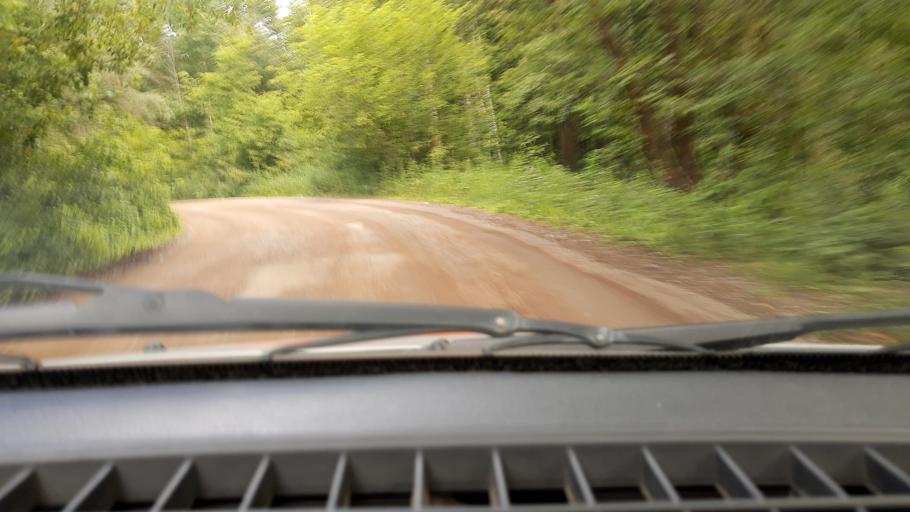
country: RU
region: Bashkortostan
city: Ufa
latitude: 54.6755
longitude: 56.0653
